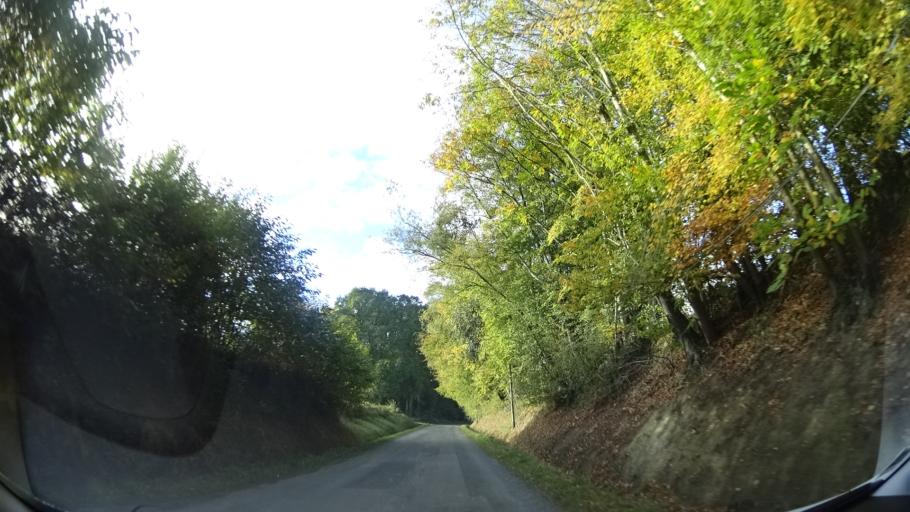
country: FR
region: Brittany
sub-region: Departement d'Ille-et-Vilaine
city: Geveze
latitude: 48.2133
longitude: -1.7966
